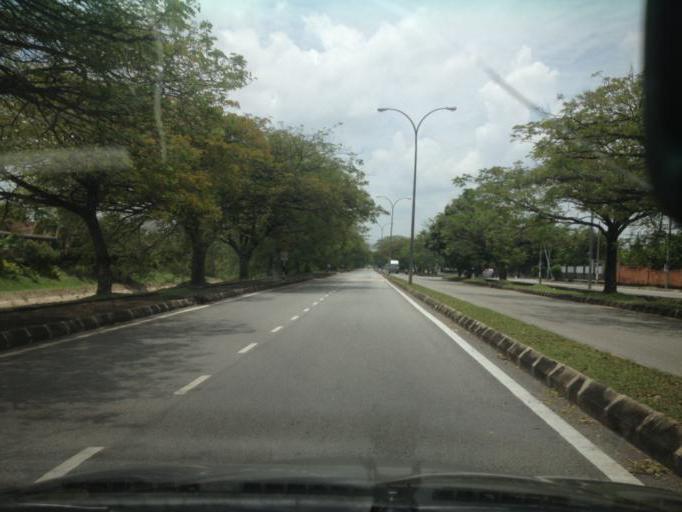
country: MY
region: Kedah
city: Sungai Petani
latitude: 5.6053
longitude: 100.5409
